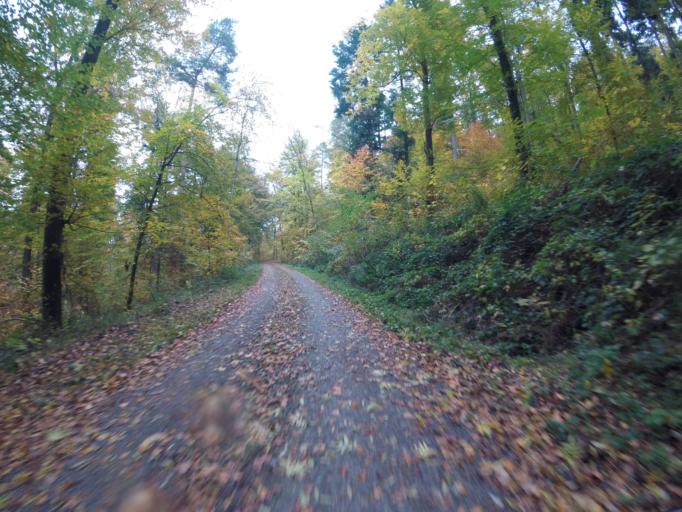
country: DE
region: Baden-Wuerttemberg
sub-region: Regierungsbezirk Stuttgart
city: Oberstenfeld
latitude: 49.0024
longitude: 9.3287
